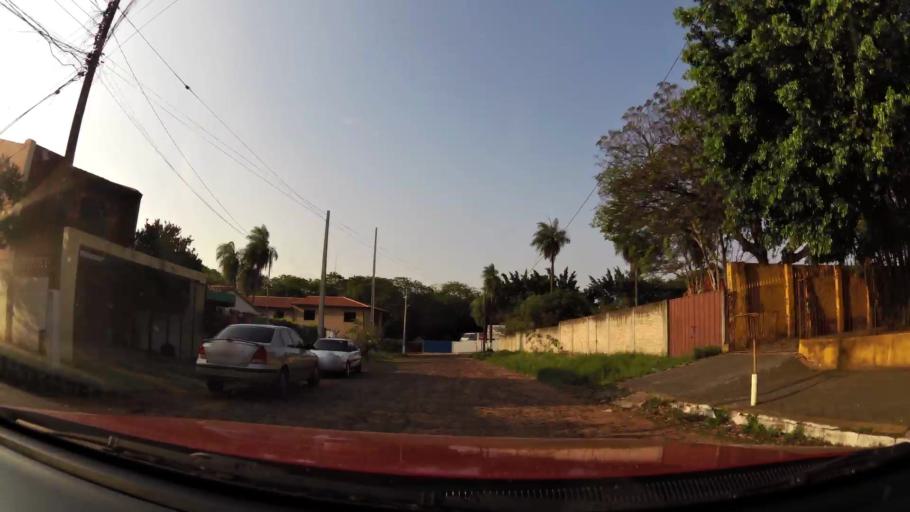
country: PY
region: Central
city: Lambare
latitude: -25.3571
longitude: -57.6014
